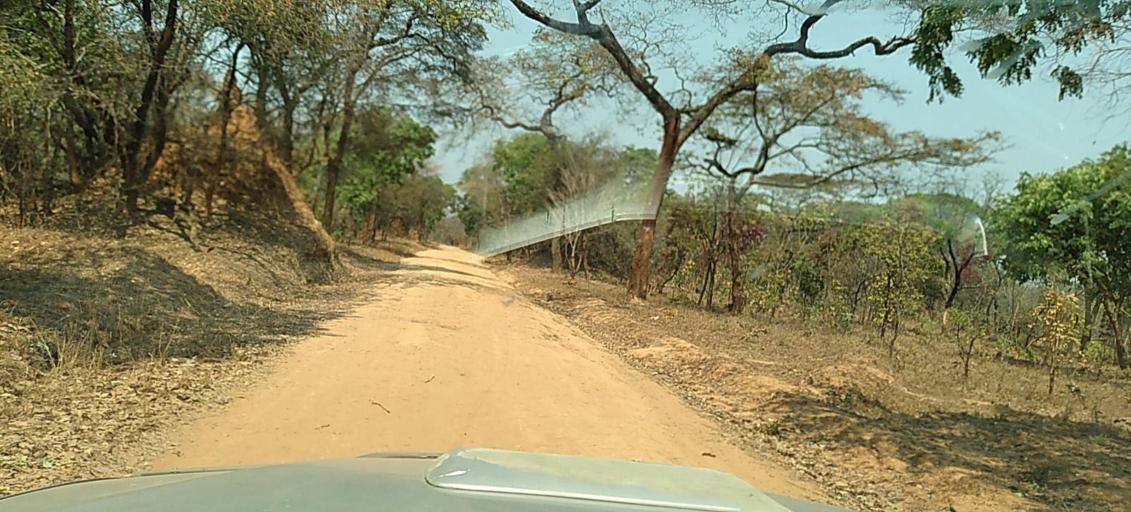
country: ZM
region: North-Western
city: Kasempa
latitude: -13.6655
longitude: 26.2837
